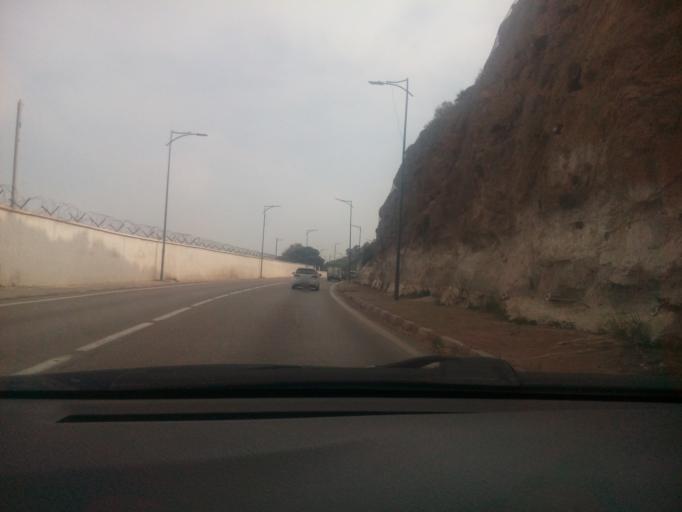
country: DZ
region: Oran
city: Oran
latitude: 35.7134
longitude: -0.6699
